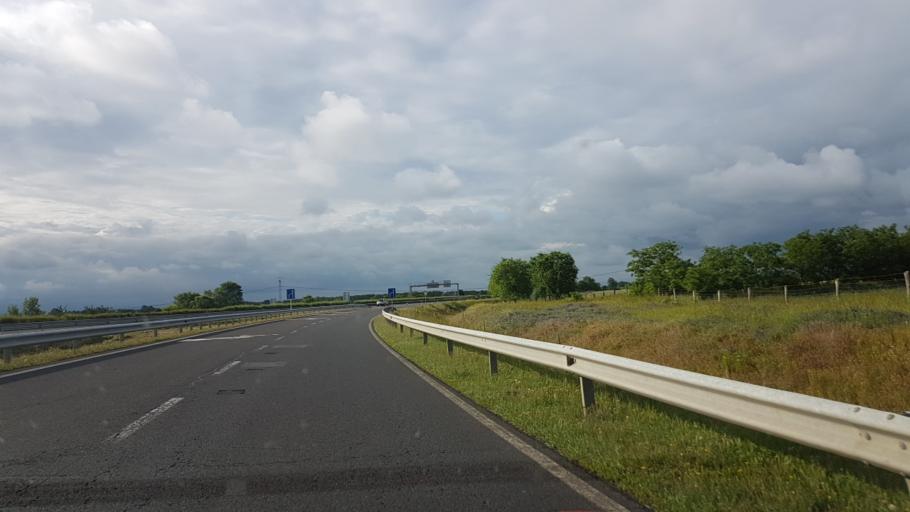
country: HU
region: Borsod-Abauj-Zemplen
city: Emod
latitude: 47.8861
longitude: 20.8341
